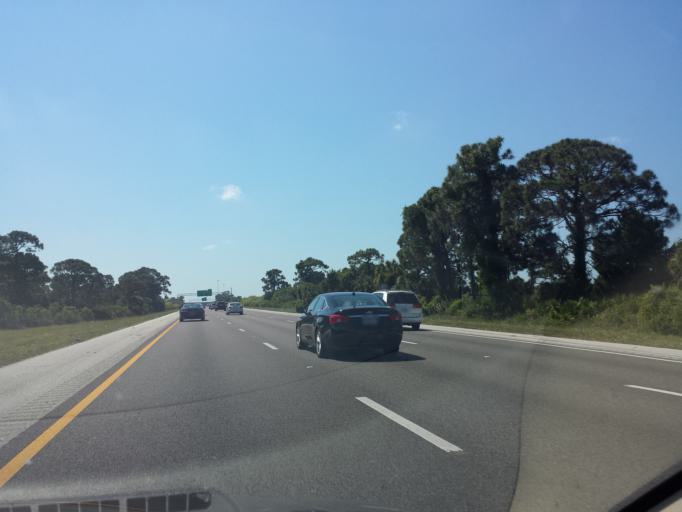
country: US
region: Florida
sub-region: Sarasota County
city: Osprey
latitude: 27.2027
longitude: -82.4419
